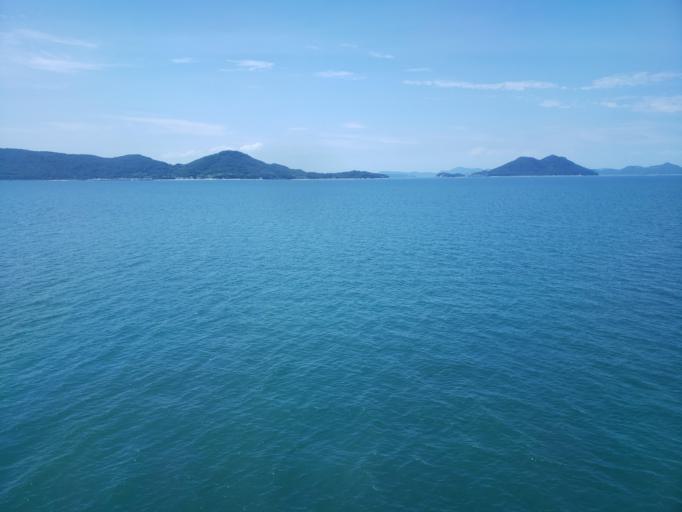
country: JP
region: Kagawa
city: Takamatsu-shi
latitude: 34.3768
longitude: 134.0827
